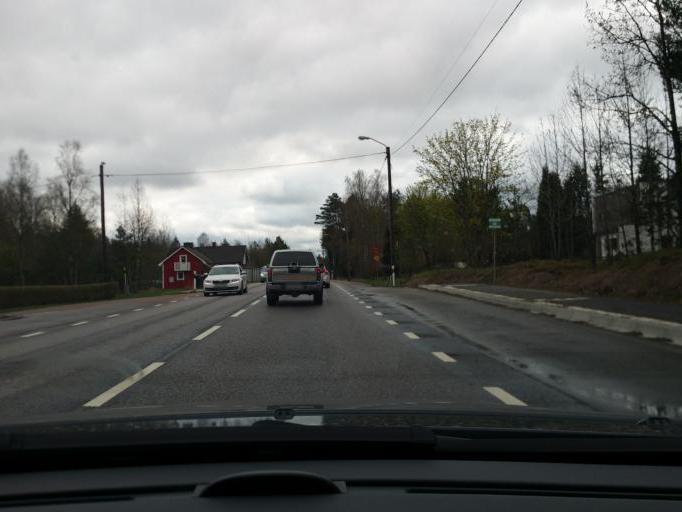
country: SE
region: Kronoberg
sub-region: Vaxjo Kommun
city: Ingelstad
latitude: 56.8236
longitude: 14.8783
